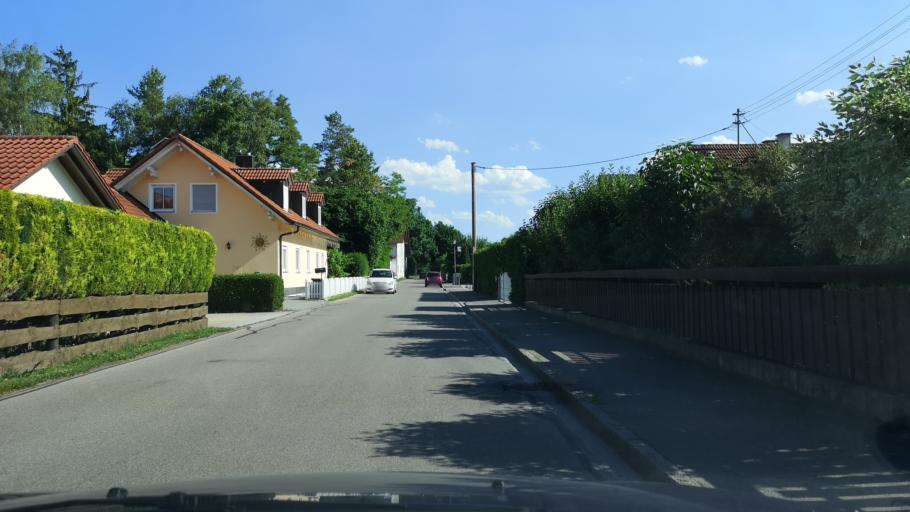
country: DE
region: Bavaria
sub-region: Upper Bavaria
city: Eichenried
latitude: 48.2407
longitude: 11.7815
